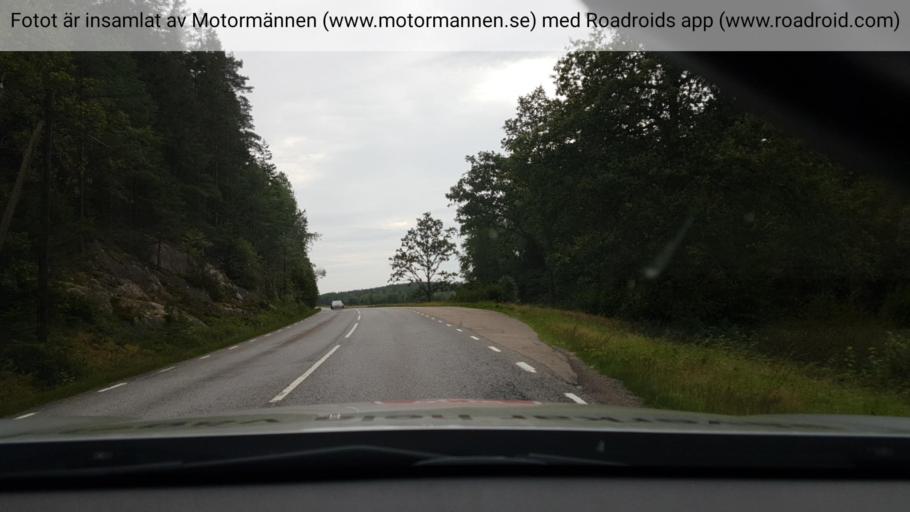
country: SE
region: Vaestra Goetaland
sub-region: Tanums Kommun
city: Tanumshede
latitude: 58.5829
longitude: 11.3561
